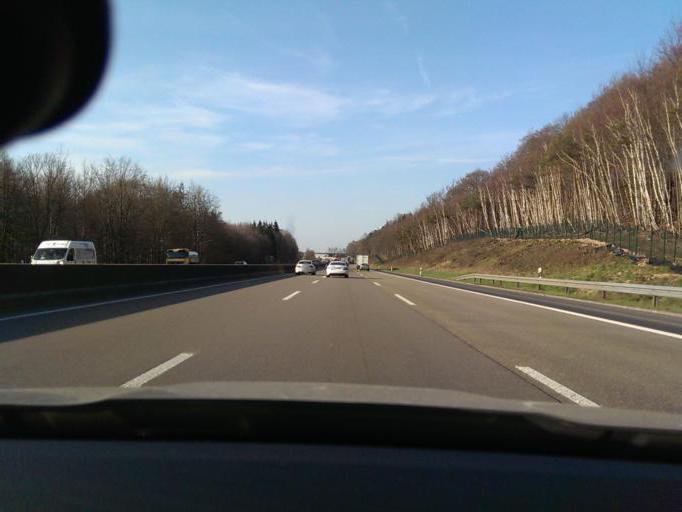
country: DE
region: Hesse
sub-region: Regierungsbezirk Kassel
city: Malsfeld
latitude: 51.0143
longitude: 9.4892
